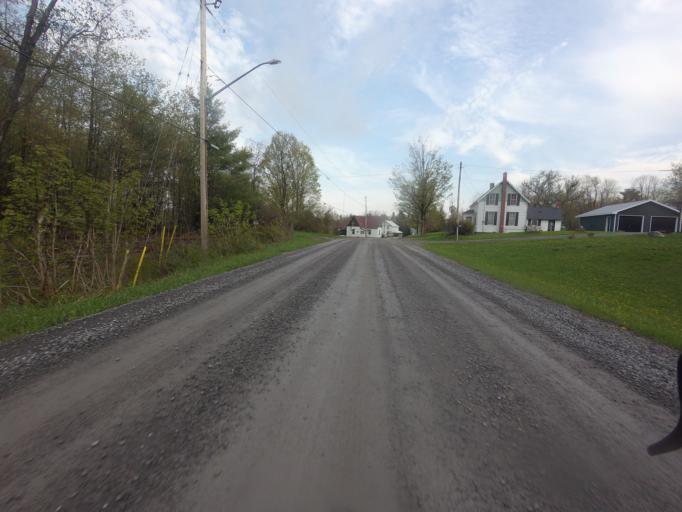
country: CA
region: Ontario
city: Carleton Place
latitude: 45.1946
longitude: -76.3265
